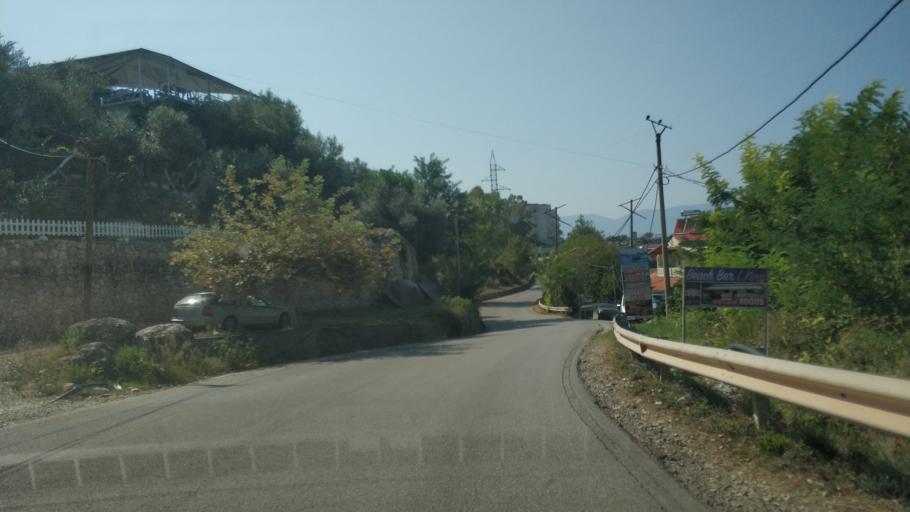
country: AL
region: Vlore
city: Vlore
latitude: 40.4021
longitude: 19.4805
